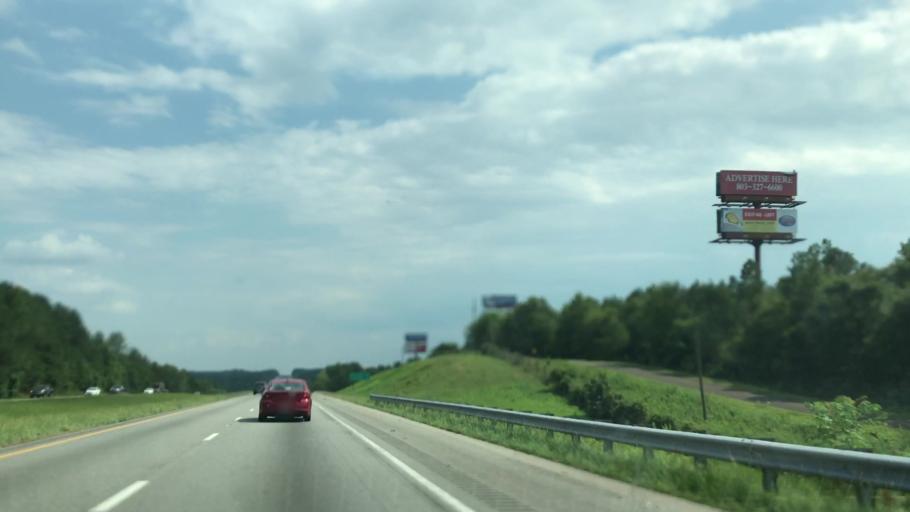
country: US
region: South Carolina
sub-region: Chester County
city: Great Falls
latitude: 34.5978
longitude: -81.0171
